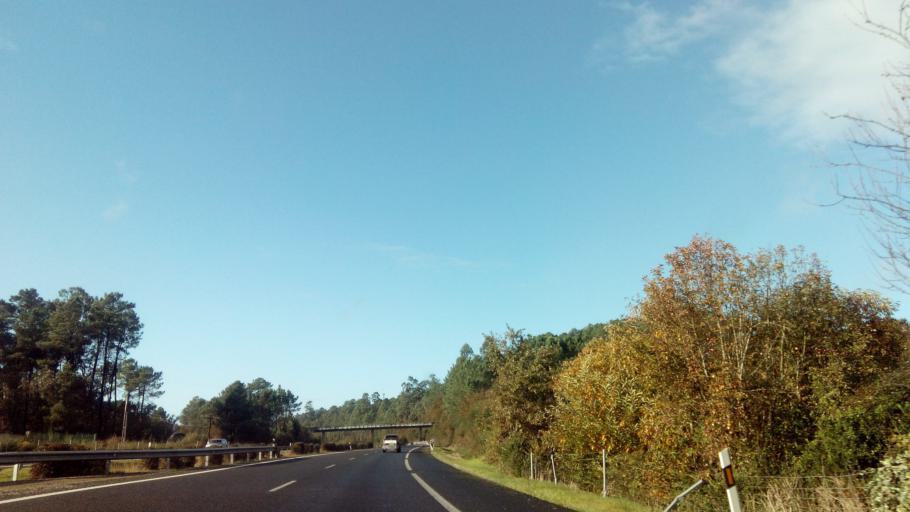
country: ES
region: Galicia
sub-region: Provincia de Pontevedra
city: Ponteareas
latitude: 42.1573
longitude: -8.5215
